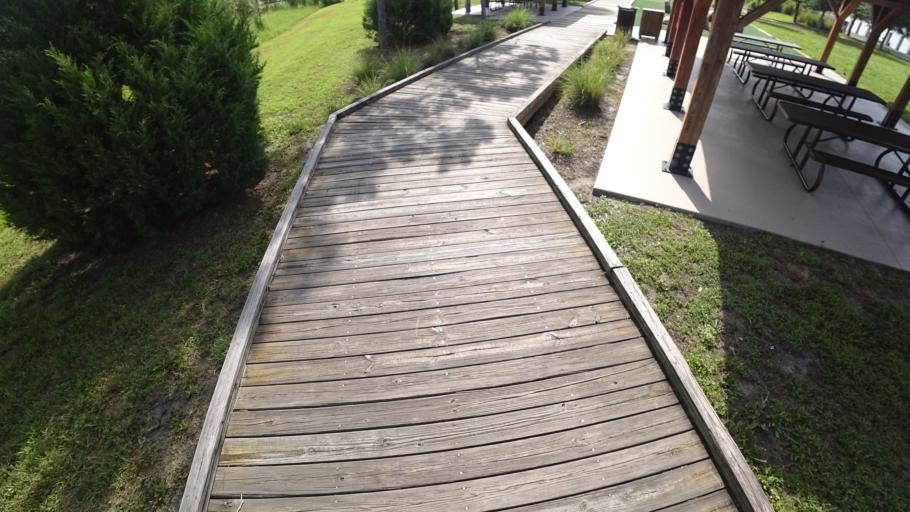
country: US
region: Florida
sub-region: Sarasota County
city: Desoto Lakes
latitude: 27.4323
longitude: -82.4821
